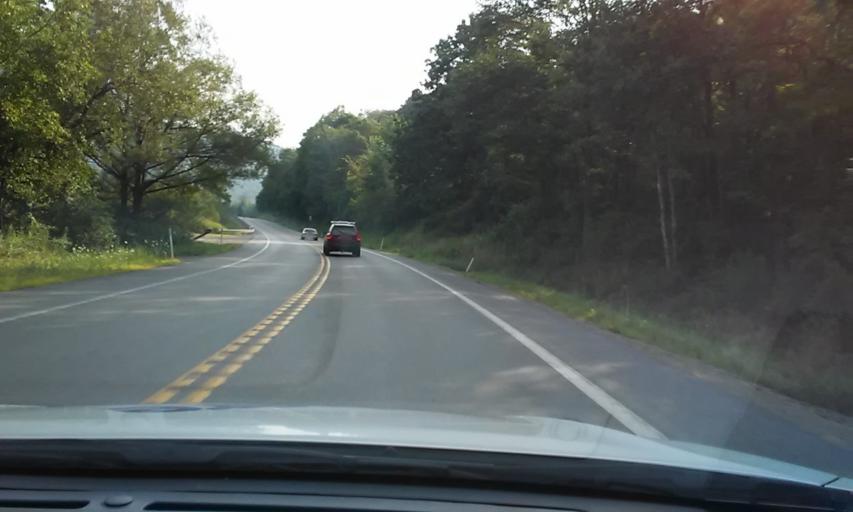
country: US
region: Pennsylvania
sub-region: Potter County
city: Coudersport
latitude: 41.7483
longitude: -78.0717
